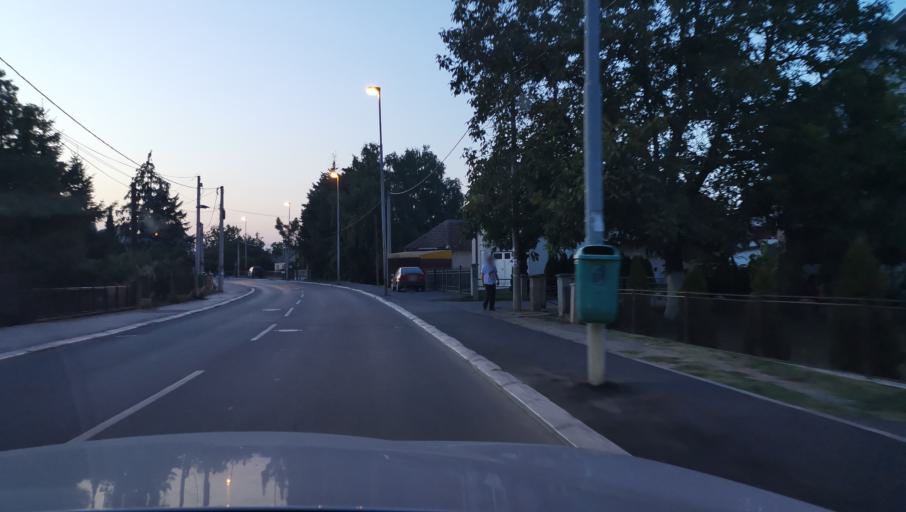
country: RS
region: Central Serbia
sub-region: Belgrade
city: Obrenovac
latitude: 44.6629
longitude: 20.2017
